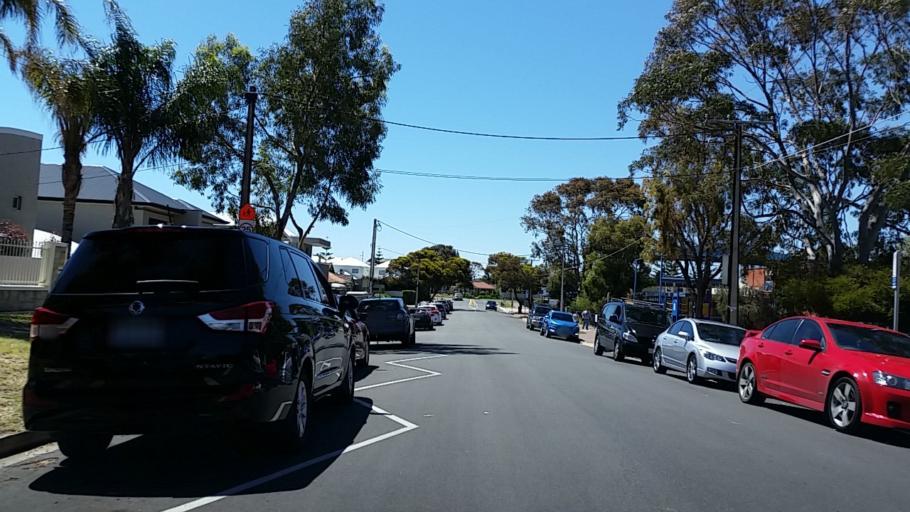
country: AU
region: South Australia
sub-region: Charles Sturt
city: Grange
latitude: -34.9037
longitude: 138.4964
